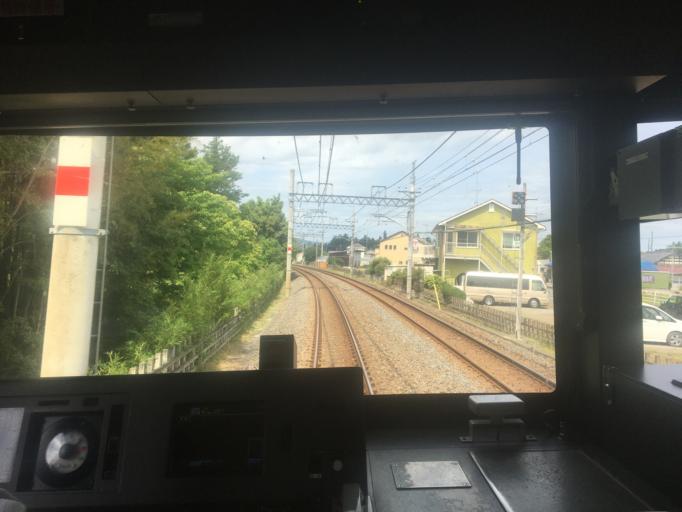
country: JP
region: Saitama
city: Kumagaya
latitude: 36.0477
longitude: 139.3593
